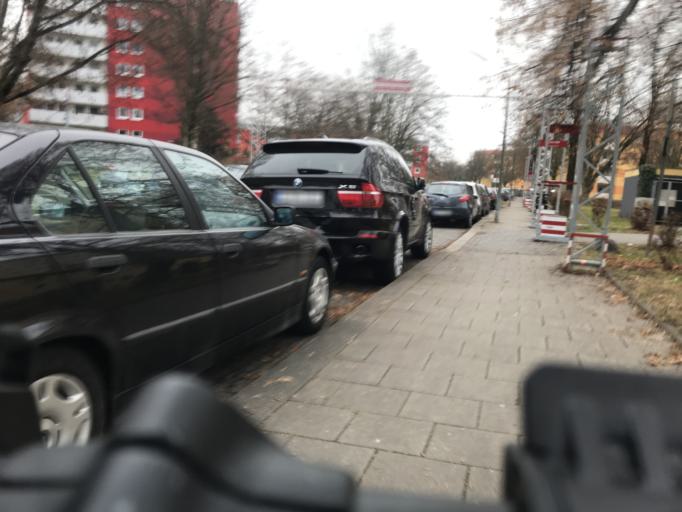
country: DE
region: Bavaria
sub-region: Upper Bavaria
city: Grafelfing
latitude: 48.1487
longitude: 11.4102
